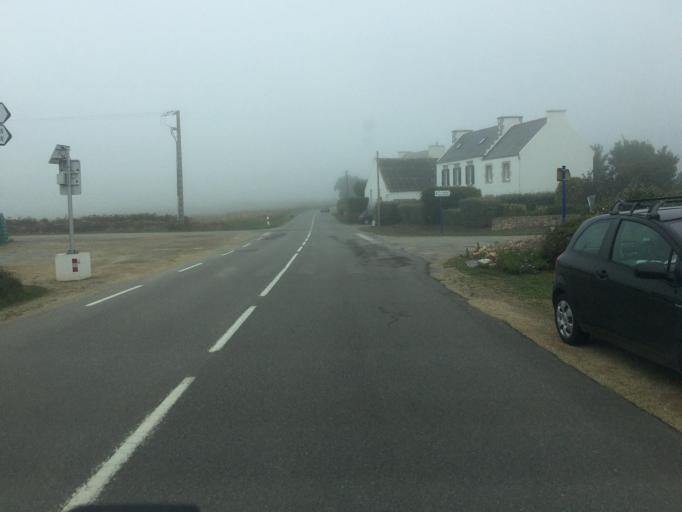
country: FR
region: Brittany
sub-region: Departement du Finistere
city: Plogoff
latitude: 48.0630
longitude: -4.6293
